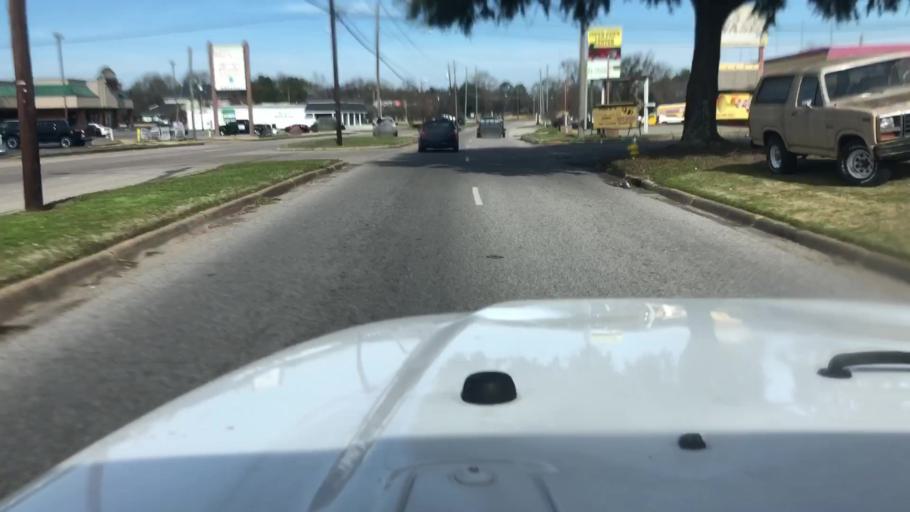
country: US
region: Alabama
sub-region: Montgomery County
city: Montgomery
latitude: 32.3840
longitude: -86.1992
